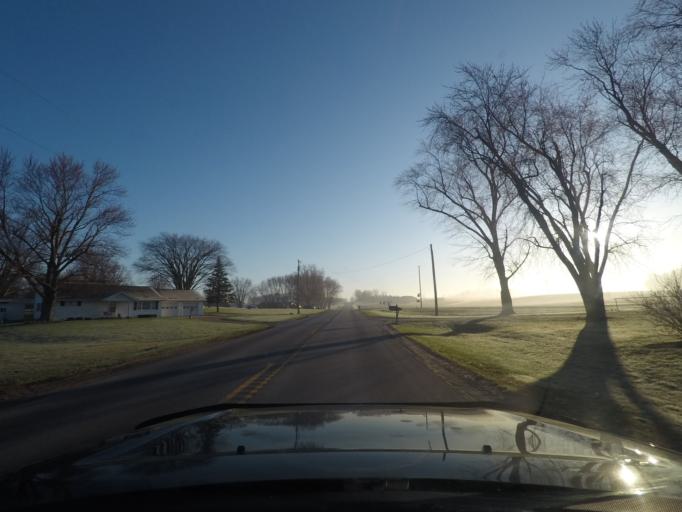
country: US
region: Indiana
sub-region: Elkhart County
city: Wakarusa
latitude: 41.5337
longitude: -85.9450
